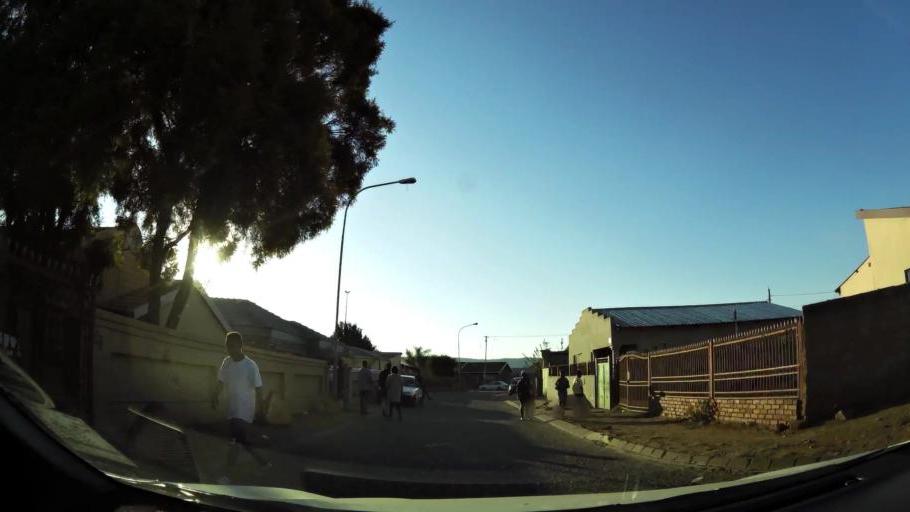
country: ZA
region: Gauteng
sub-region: City of Tshwane Metropolitan Municipality
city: Cullinan
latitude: -25.7240
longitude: 28.3803
